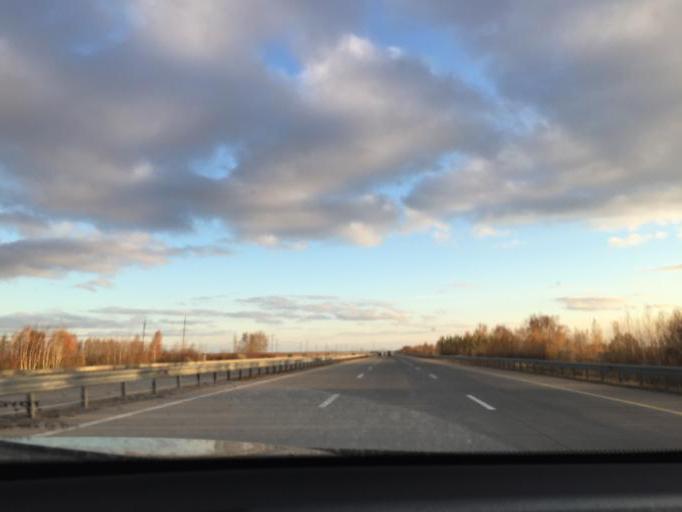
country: KZ
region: Astana Qalasy
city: Astana
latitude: 51.3302
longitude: 71.3442
